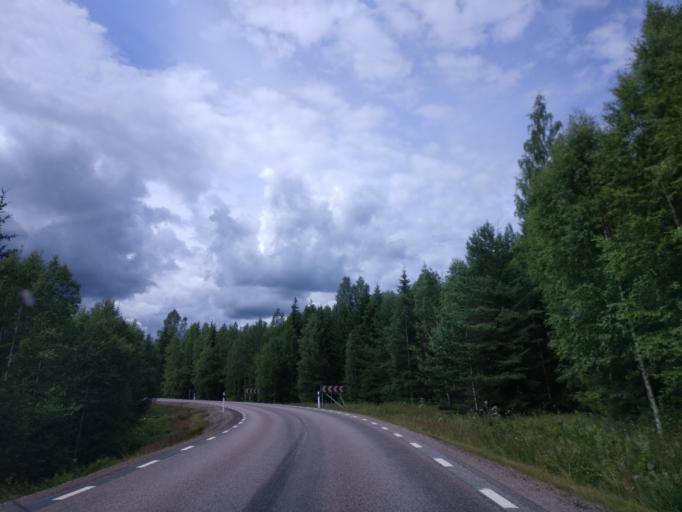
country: SE
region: Vaermland
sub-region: Hagfors Kommun
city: Ekshaerad
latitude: 60.1816
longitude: 13.3695
